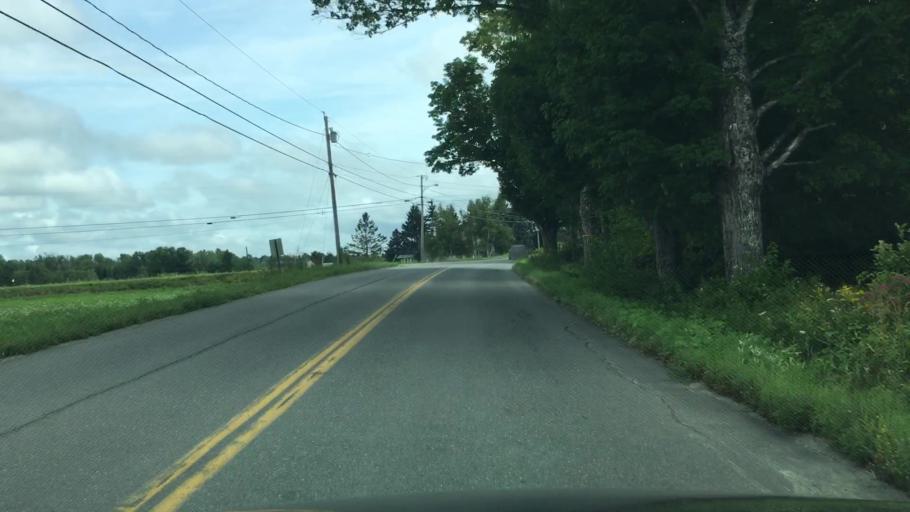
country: US
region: Maine
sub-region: Waldo County
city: Winterport
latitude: 44.6802
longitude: -68.8678
